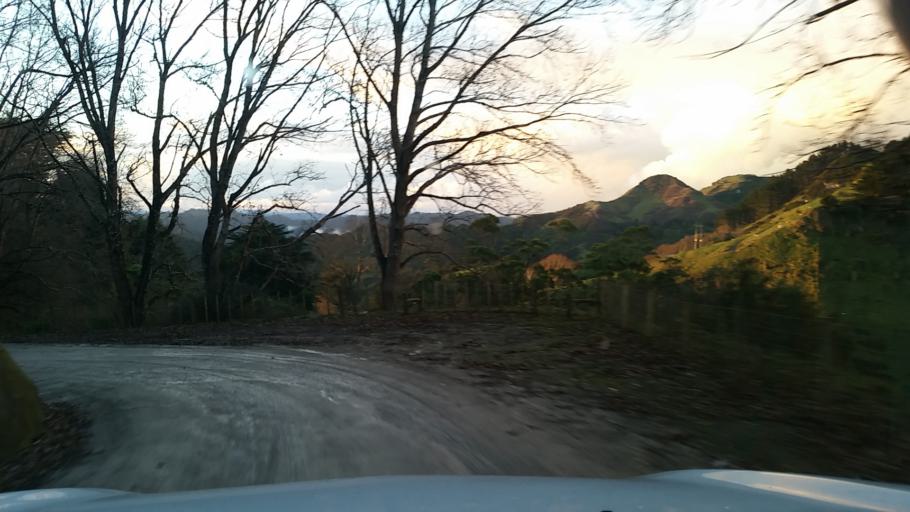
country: NZ
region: Manawatu-Wanganui
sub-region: Wanganui District
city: Wanganui
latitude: -39.7693
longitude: 174.8720
